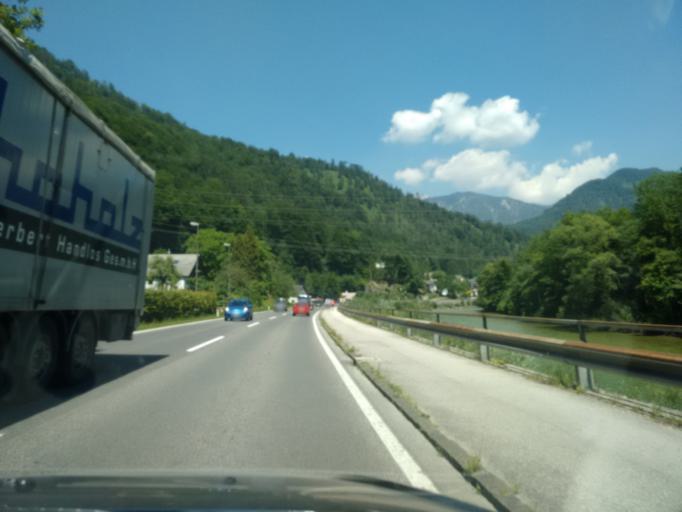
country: AT
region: Upper Austria
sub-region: Politischer Bezirk Gmunden
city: Bad Ischl
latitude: 47.7352
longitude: 13.6581
